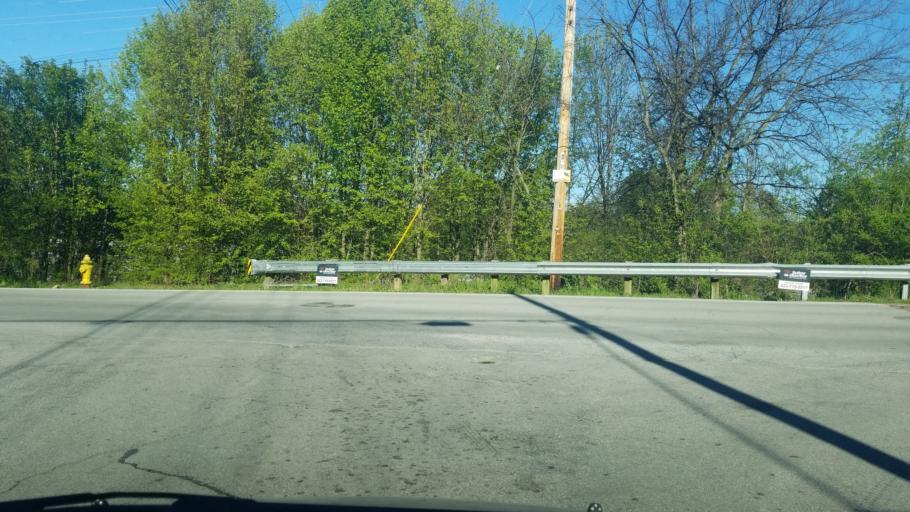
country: US
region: Tennessee
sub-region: Hamilton County
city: East Brainerd
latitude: 35.0304
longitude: -85.1678
